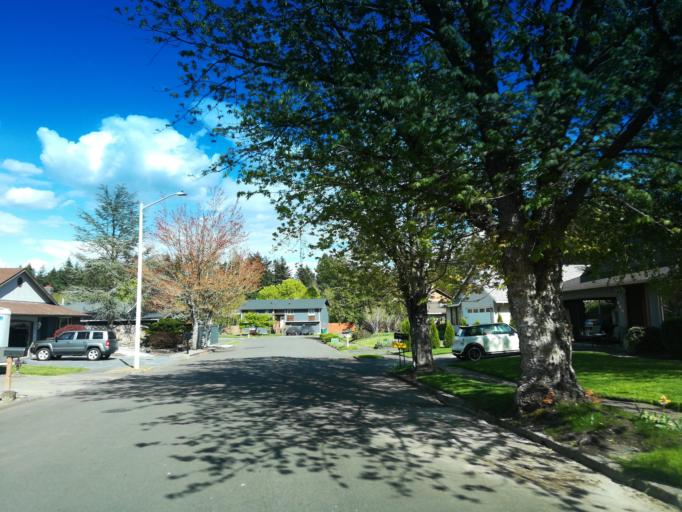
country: US
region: Oregon
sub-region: Multnomah County
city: Troutdale
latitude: 45.5279
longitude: -122.3835
